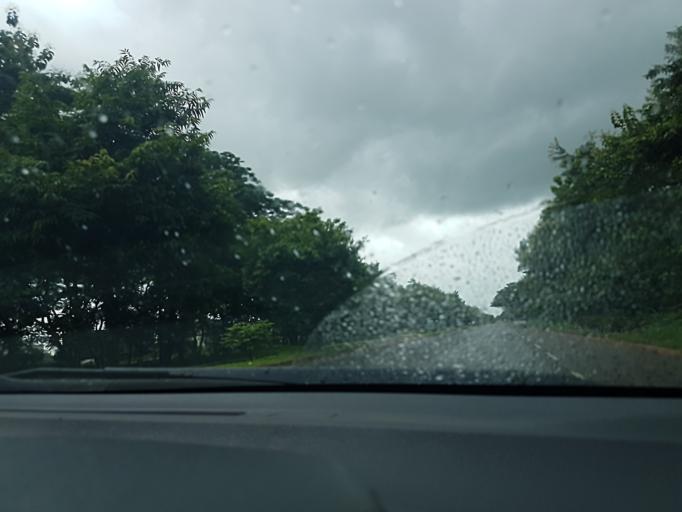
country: MM
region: Bago
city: Thanatpin
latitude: 17.1171
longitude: 96.2576
